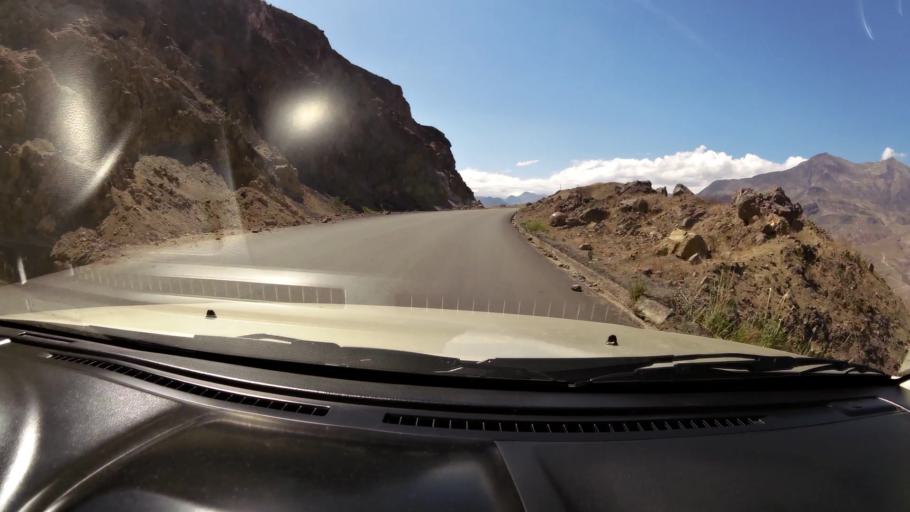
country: EC
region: El Oro
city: Zaruma
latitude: -3.3351
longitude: -79.3764
